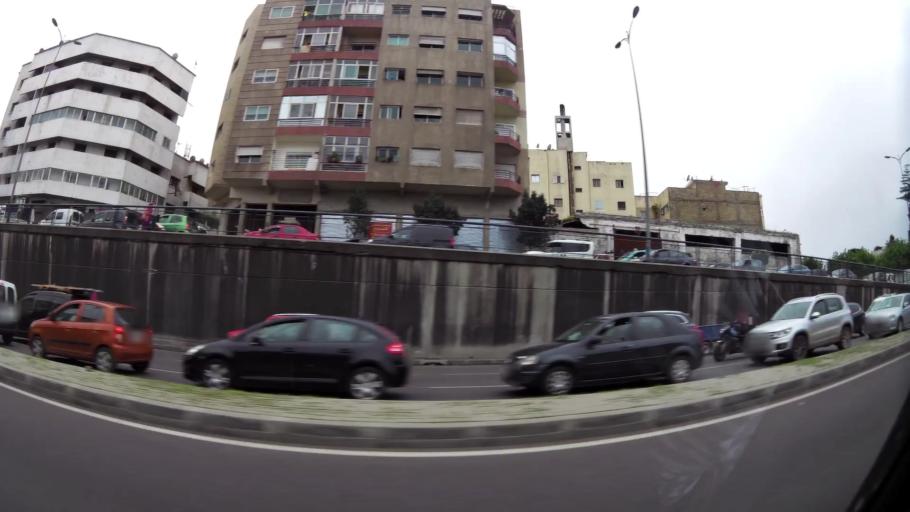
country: MA
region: Grand Casablanca
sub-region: Casablanca
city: Casablanca
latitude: 33.5786
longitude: -7.5893
